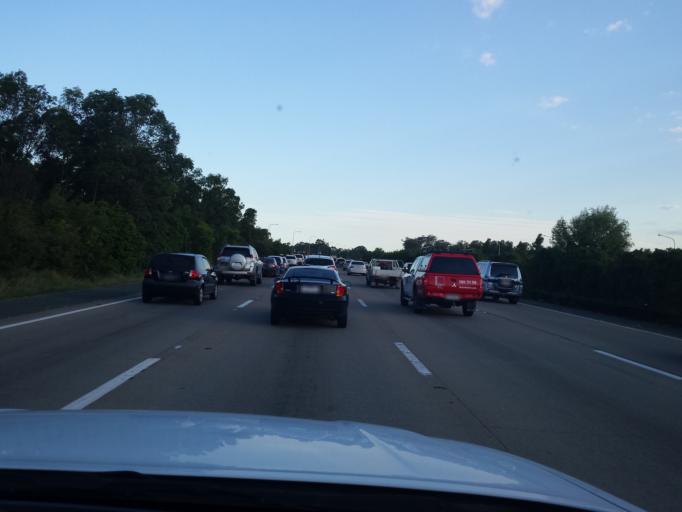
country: AU
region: Queensland
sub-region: Gold Coast
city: Oxenford
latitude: -27.8615
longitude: 153.3107
